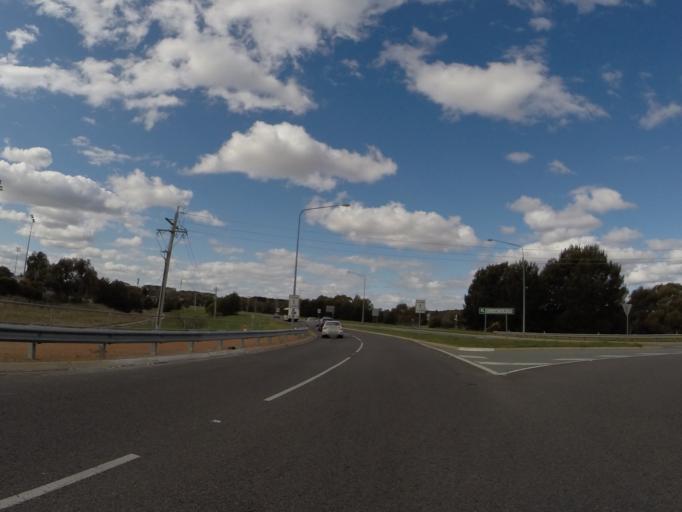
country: AU
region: Australian Capital Territory
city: Belconnen
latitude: -35.2161
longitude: 149.0844
